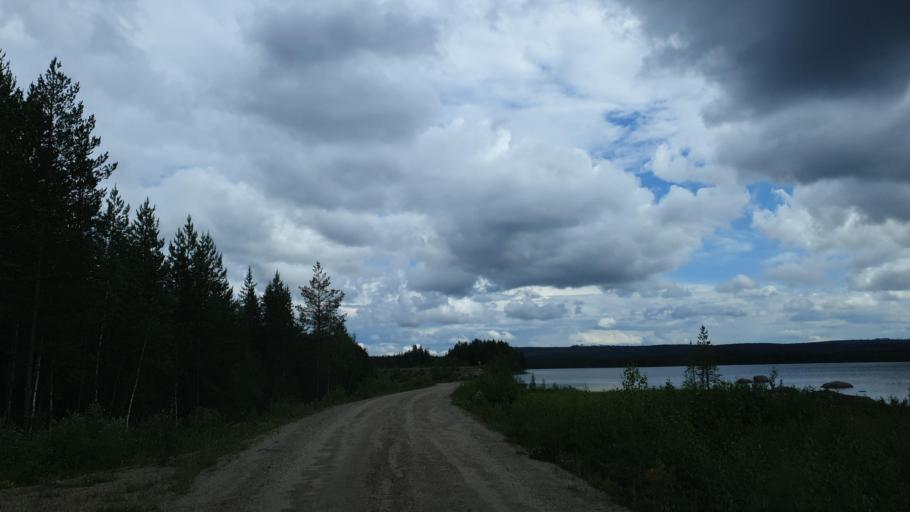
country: SE
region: Jaemtland
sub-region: Harjedalens Kommun
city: Sveg
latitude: 62.0425
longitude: 14.4831
